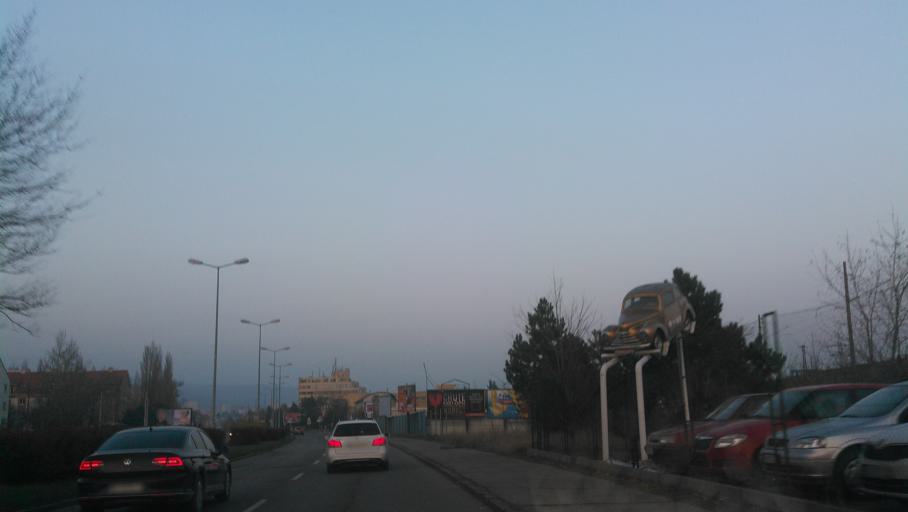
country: SK
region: Bratislavsky
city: Bratislava
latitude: 48.1978
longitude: 17.1465
